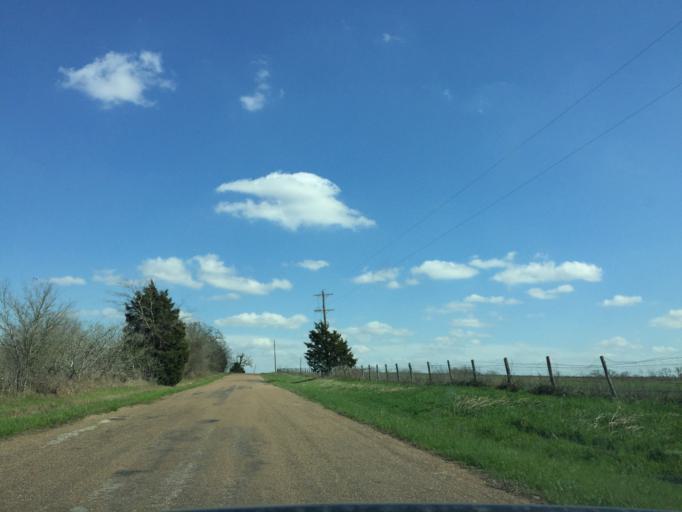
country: US
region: Texas
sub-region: Milam County
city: Thorndale
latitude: 30.5522
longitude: -97.1502
